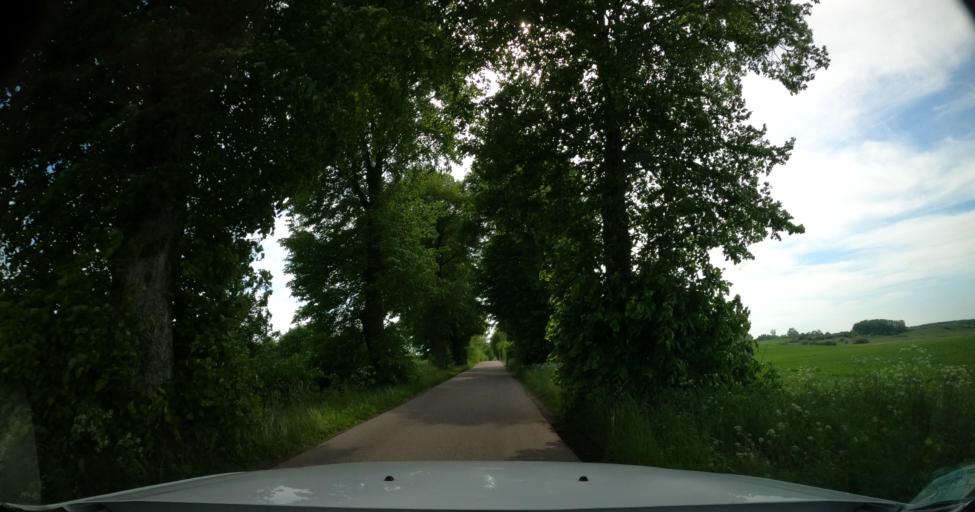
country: PL
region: Warmian-Masurian Voivodeship
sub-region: Powiat lidzbarski
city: Lubomino
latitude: 54.0816
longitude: 20.2706
